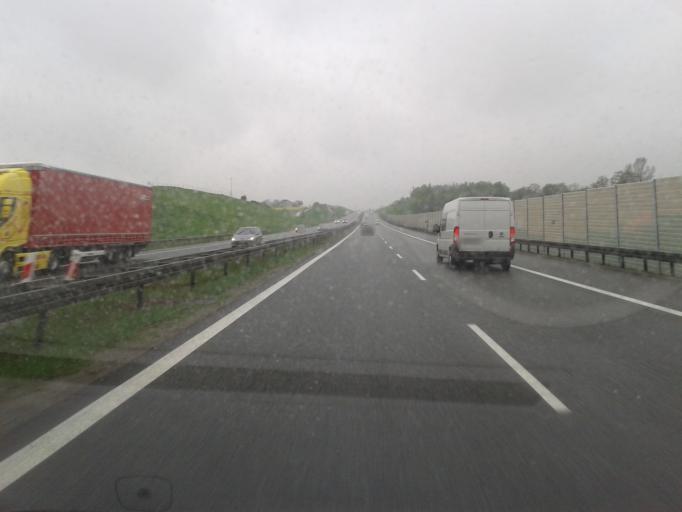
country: PL
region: Lesser Poland Voivodeship
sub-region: Powiat wielicki
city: Podleze
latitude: 49.9978
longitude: 20.2073
